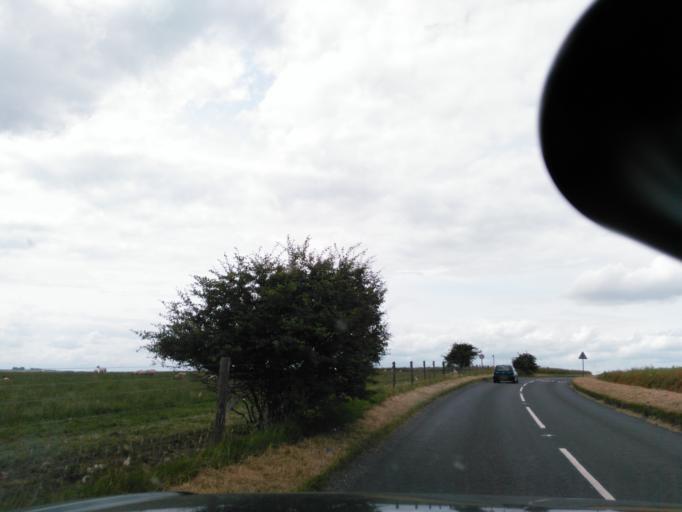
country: GB
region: England
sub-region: Wiltshire
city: Shrewton
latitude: 51.2007
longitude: -1.9181
